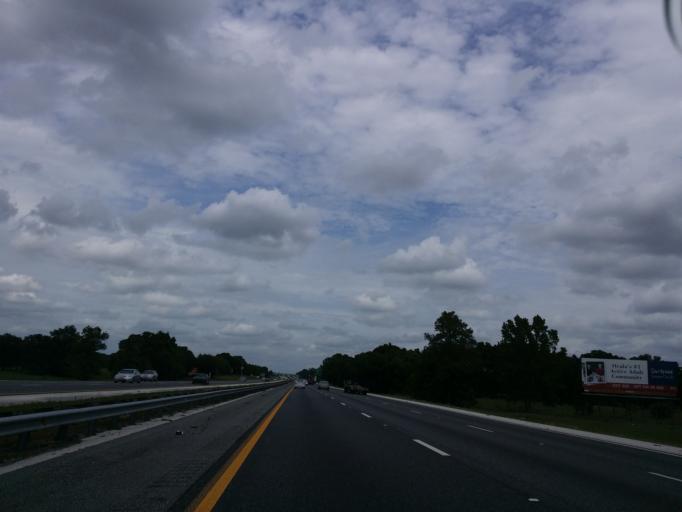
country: US
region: Florida
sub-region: Marion County
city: Ocala
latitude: 29.1262
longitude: -82.1847
